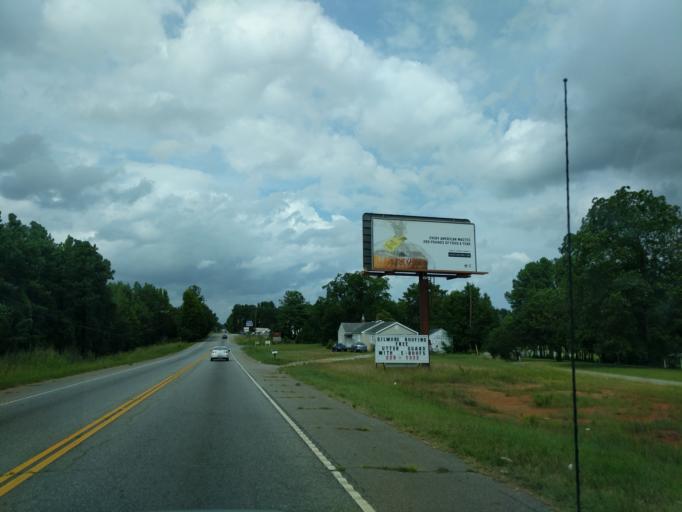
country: US
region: South Carolina
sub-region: Anderson County
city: Anderson
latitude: 34.5269
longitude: -82.5901
